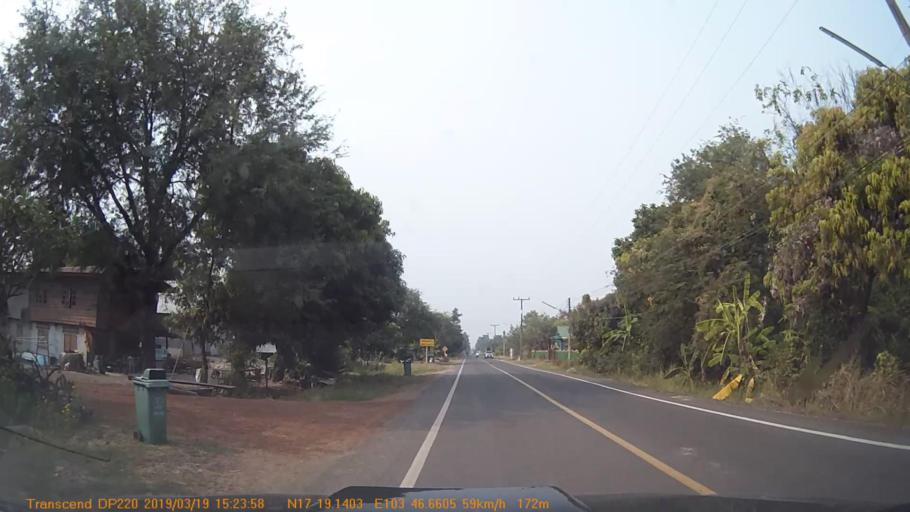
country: TH
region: Sakon Nakhon
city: Phanna Nikhom
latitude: 17.3192
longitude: 103.7777
